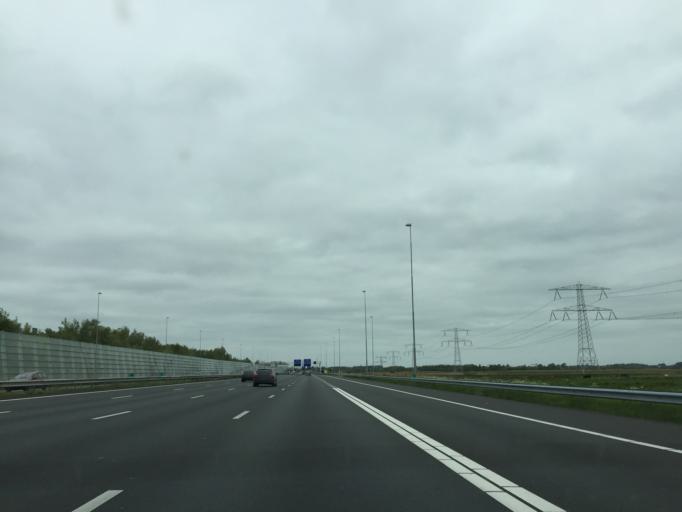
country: NL
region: North Holland
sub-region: Gemeente Zaanstad
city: Zaandam
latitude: 52.4443
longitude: 4.8544
